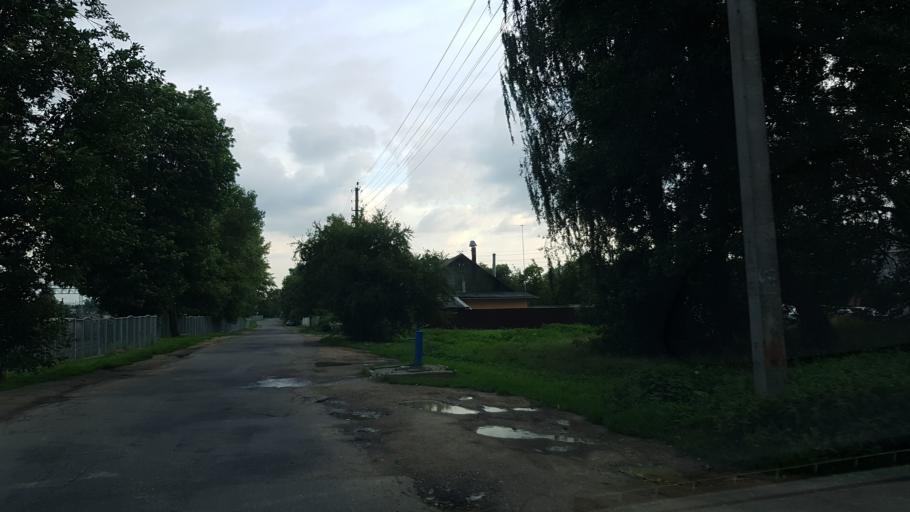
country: BY
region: Minsk
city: Syenitsa
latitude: 53.8705
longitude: 27.5188
